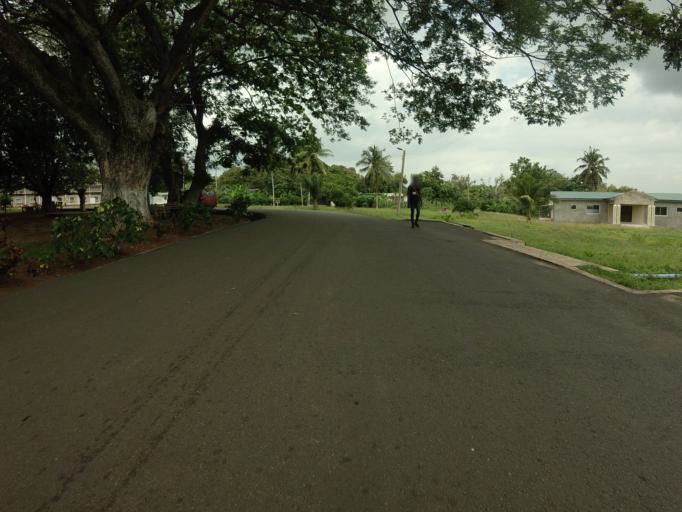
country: GH
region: Volta
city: Ho
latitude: 6.5977
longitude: 0.4735
